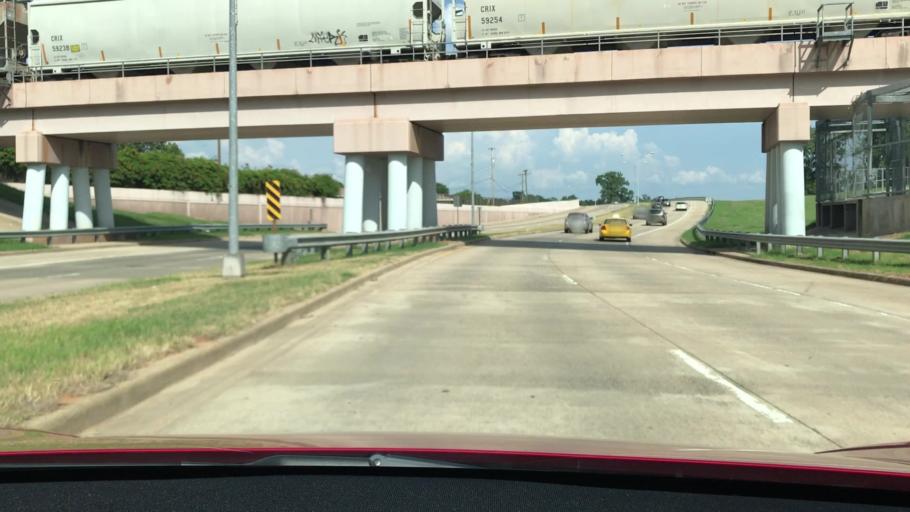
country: US
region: Louisiana
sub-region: Bossier Parish
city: Bossier City
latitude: 32.5113
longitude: -93.7236
